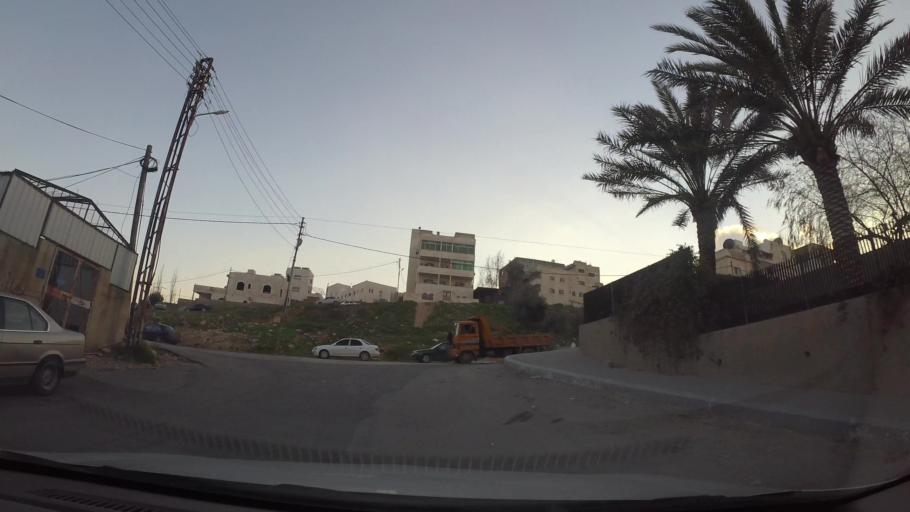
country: JO
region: Amman
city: Al Bunayyat ash Shamaliyah
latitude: 31.9065
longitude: 35.9191
